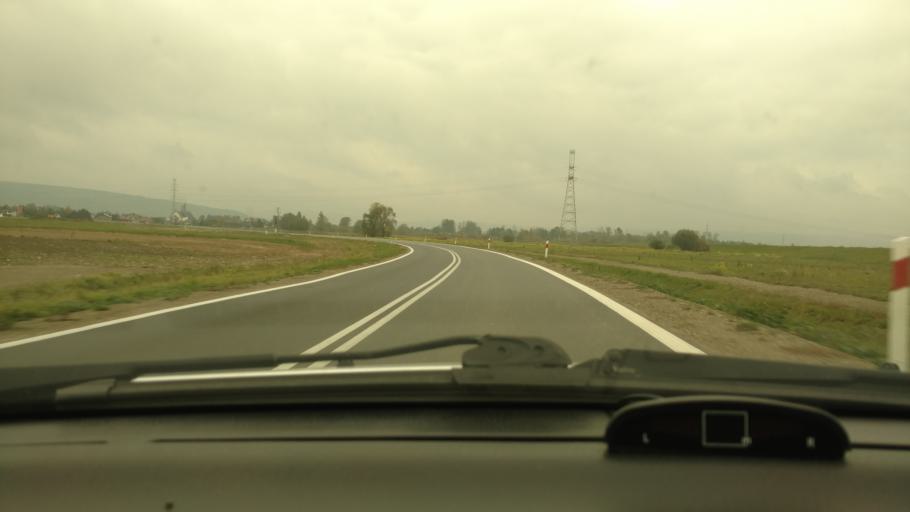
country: PL
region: Lesser Poland Voivodeship
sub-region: Powiat nowosadecki
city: Stary Sacz
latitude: 49.5936
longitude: 20.6471
